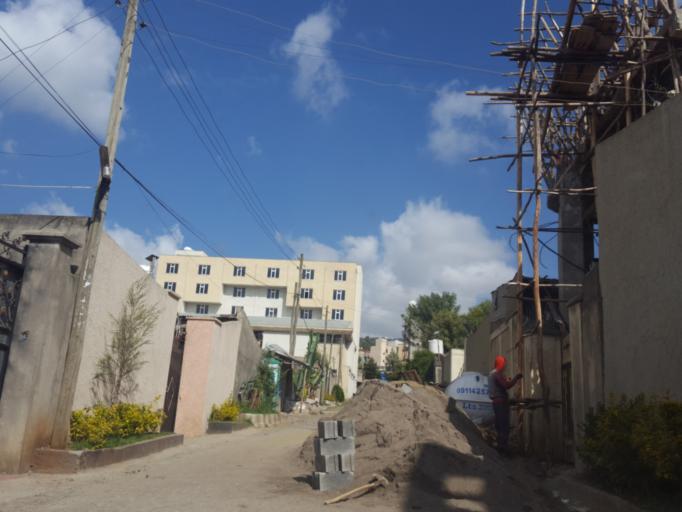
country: ET
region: Adis Abeba
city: Addis Ababa
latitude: 9.0680
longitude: 38.7191
